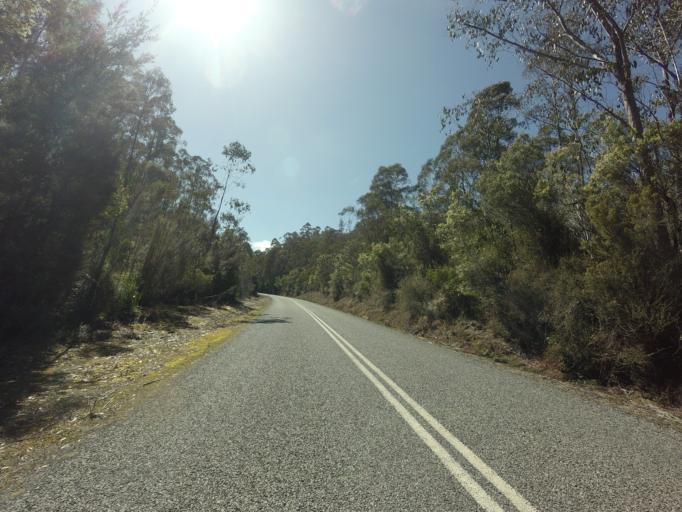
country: AU
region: Tasmania
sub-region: Derwent Valley
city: New Norfolk
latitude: -42.7581
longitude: 146.4062
